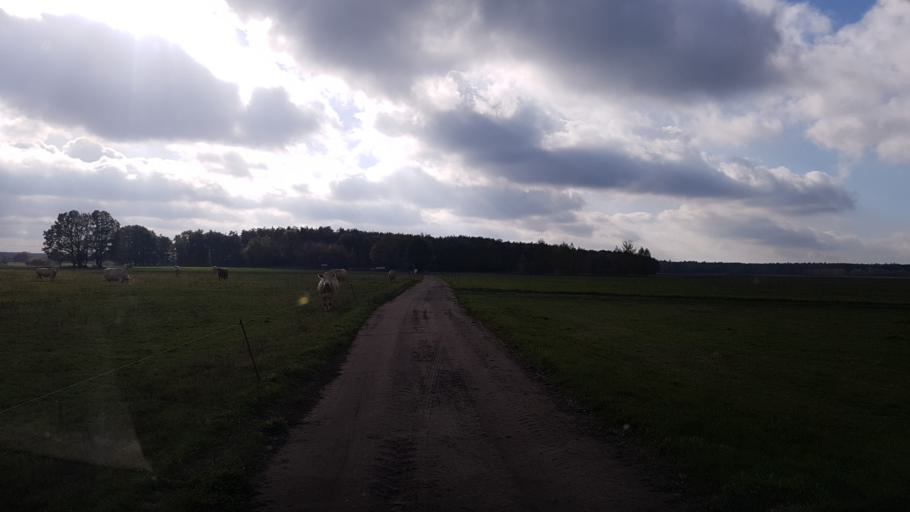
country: DE
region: Brandenburg
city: Schonborn
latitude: 51.5835
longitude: 13.5157
